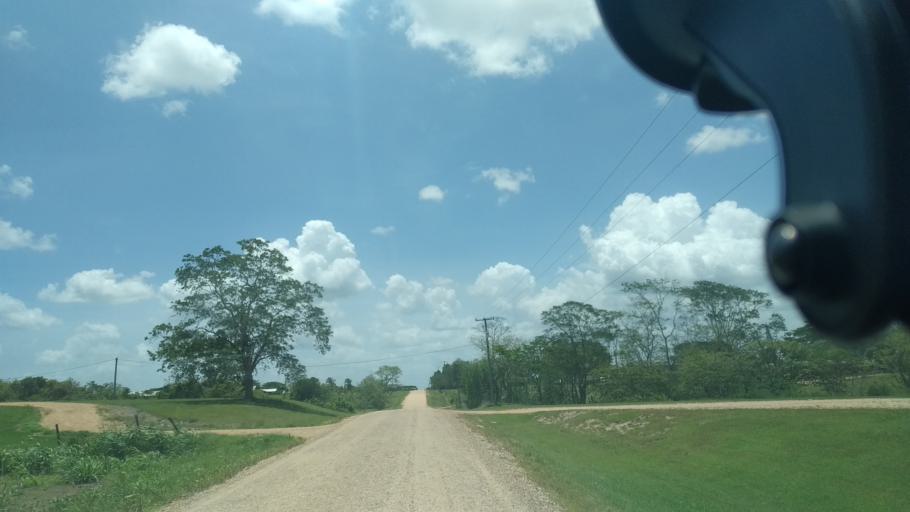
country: BZ
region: Cayo
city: San Ignacio
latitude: 17.2329
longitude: -88.9876
